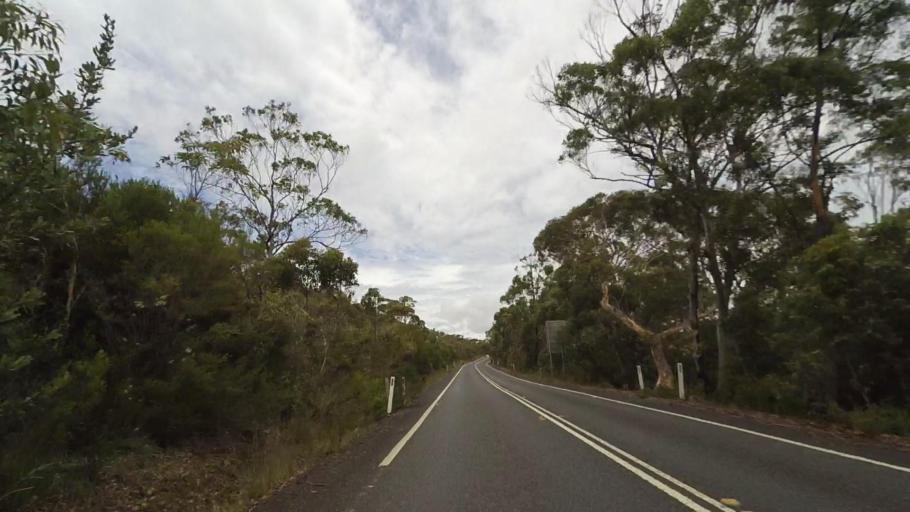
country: AU
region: New South Wales
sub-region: Sutherland Shire
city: Grays Point
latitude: -34.1164
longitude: 151.0695
